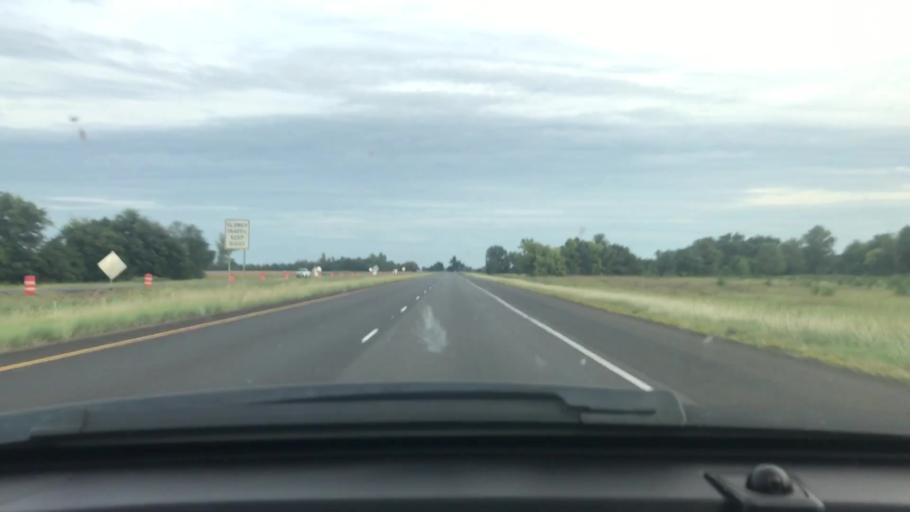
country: US
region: Arkansas
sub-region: Poinsett County
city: Trumann
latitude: 35.6685
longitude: -90.5523
